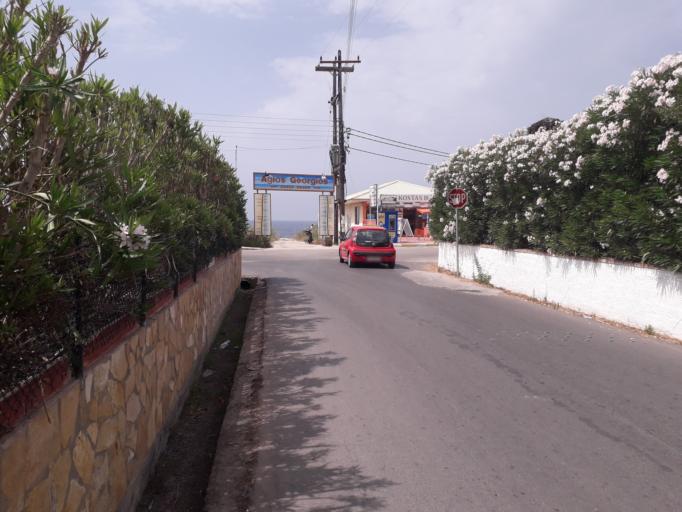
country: GR
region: Ionian Islands
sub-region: Nomos Kerkyras
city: Perivoli
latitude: 39.4261
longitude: 19.9475
